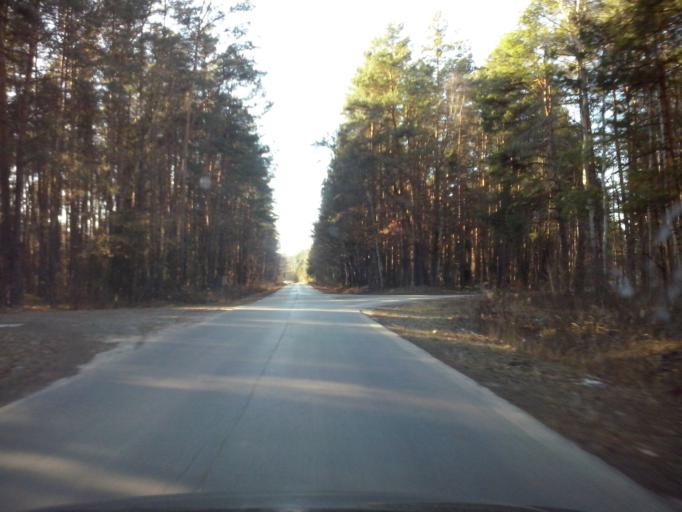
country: PL
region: Subcarpathian Voivodeship
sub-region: Powiat nizanski
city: Harasiuki
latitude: 50.5320
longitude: 22.4486
